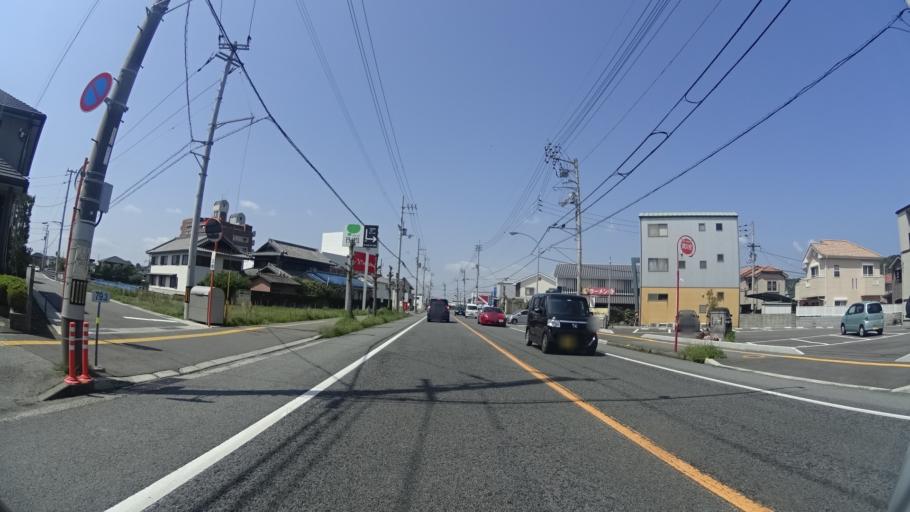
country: JP
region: Tokushima
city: Narutocho-mitsuishi
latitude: 34.1711
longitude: 134.6055
